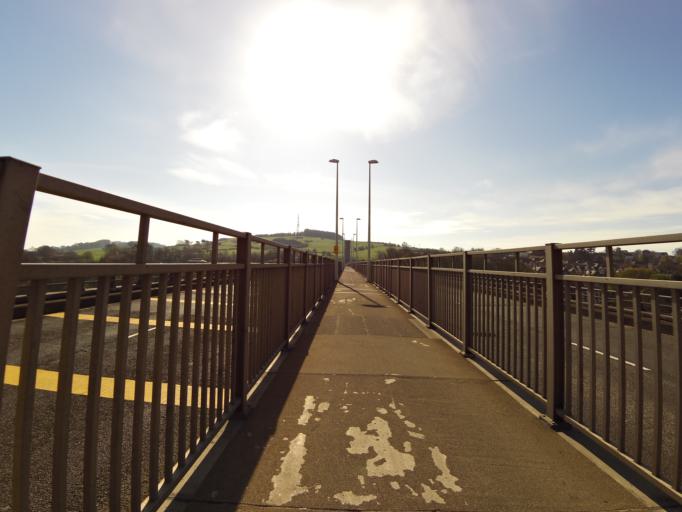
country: GB
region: Scotland
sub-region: Fife
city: Newport-On-Tay
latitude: 56.4480
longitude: -2.9361
